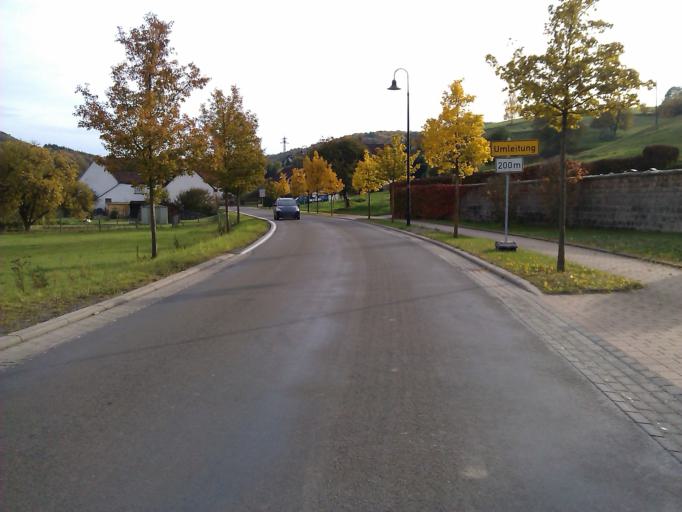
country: DE
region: Rheinland-Pfalz
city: Hefersweiler
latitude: 49.6088
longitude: 7.6855
